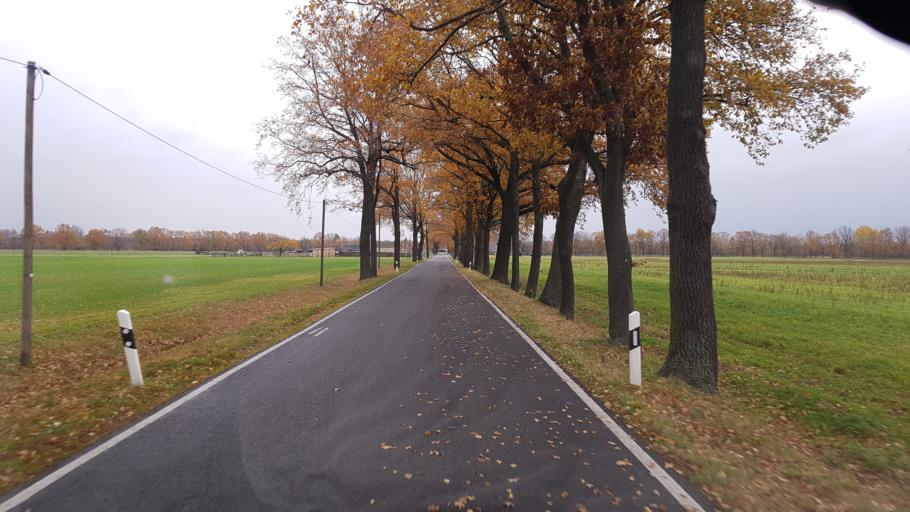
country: DE
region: Brandenburg
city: Schraden
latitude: 51.4302
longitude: 13.7110
